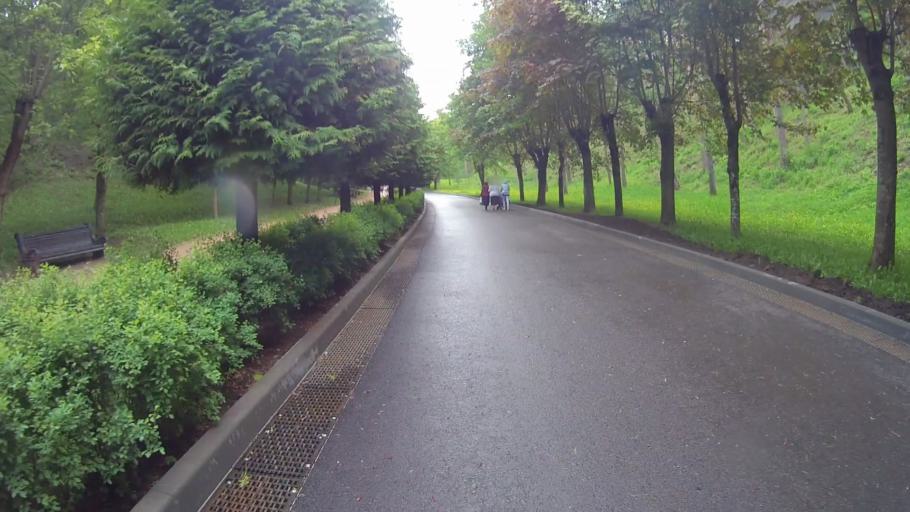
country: RU
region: Stavropol'skiy
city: Kislovodsk
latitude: 43.8956
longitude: 42.7251
